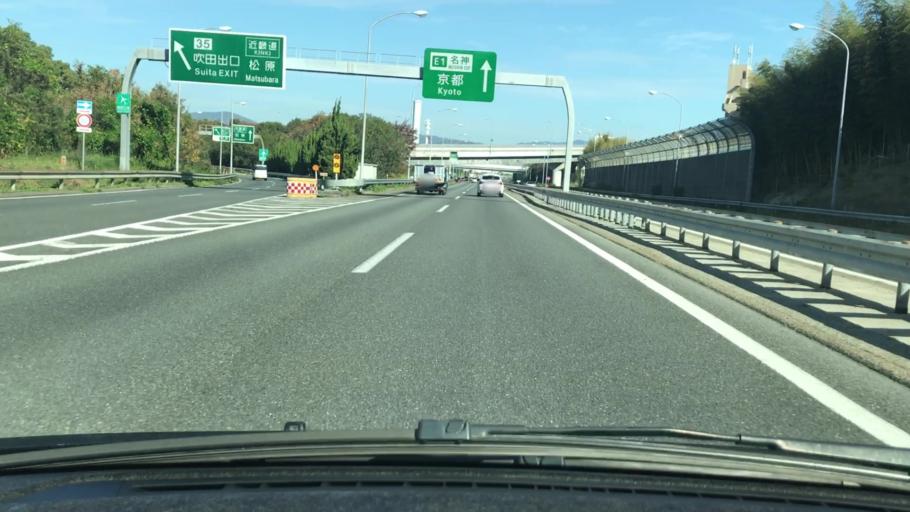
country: JP
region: Osaka
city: Ibaraki
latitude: 34.8009
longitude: 135.5404
